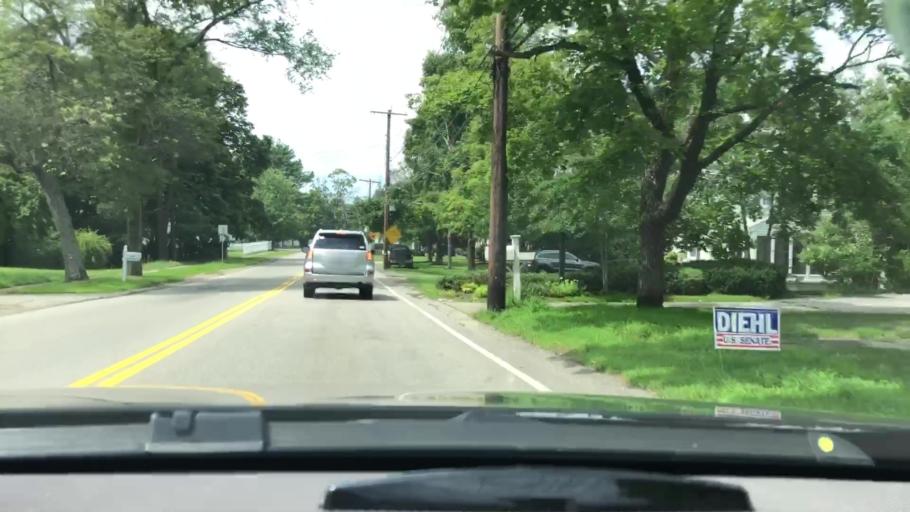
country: US
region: Massachusetts
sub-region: Norfolk County
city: Walpole
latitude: 42.1471
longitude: -71.2338
